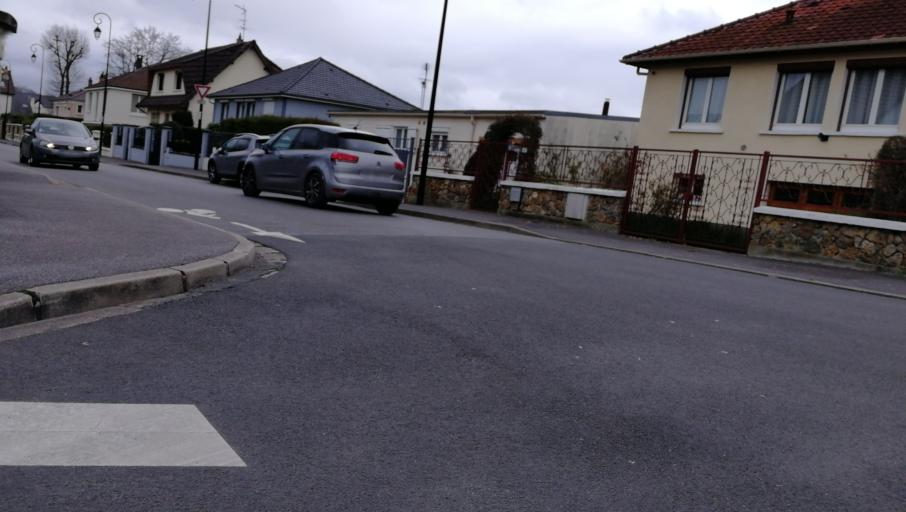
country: FR
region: Ile-de-France
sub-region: Departement du Val-de-Marne
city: Le Plessis-Trevise
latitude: 48.8034
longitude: 2.5818
